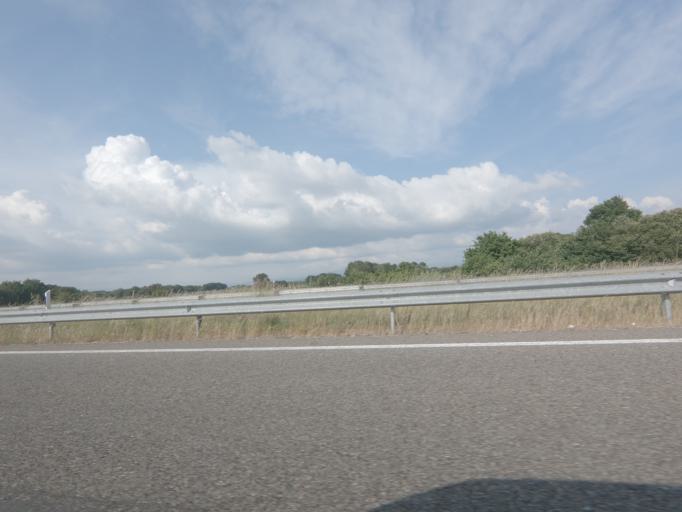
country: ES
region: Galicia
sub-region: Provincia de Ourense
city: Xinzo de Limia
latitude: 42.1094
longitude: -7.7355
